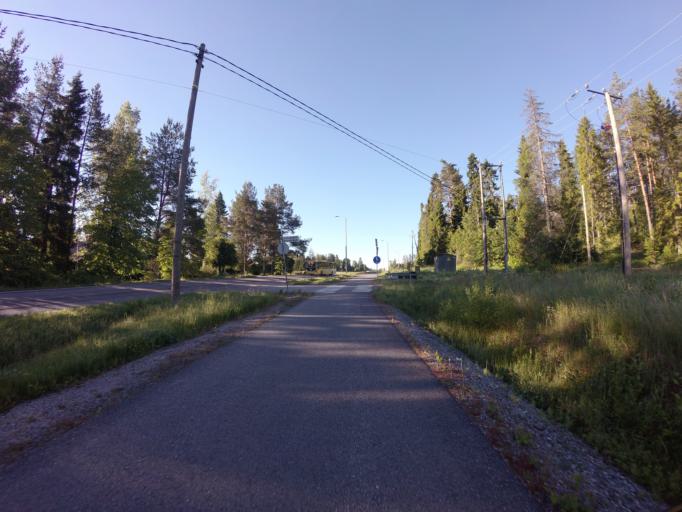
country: FI
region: Varsinais-Suomi
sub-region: Turku
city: Vahto
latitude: 60.5331
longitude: 22.3444
